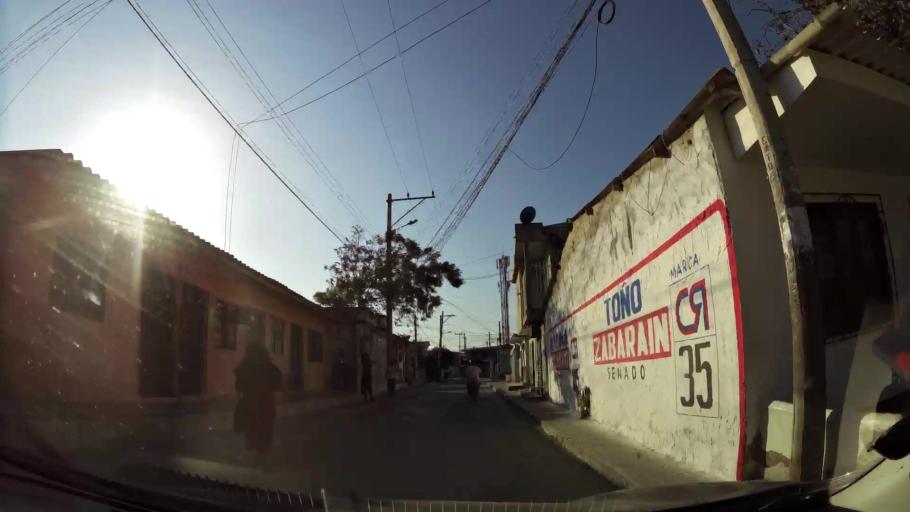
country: CO
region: Atlantico
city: Barranquilla
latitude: 11.0404
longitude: -74.8271
